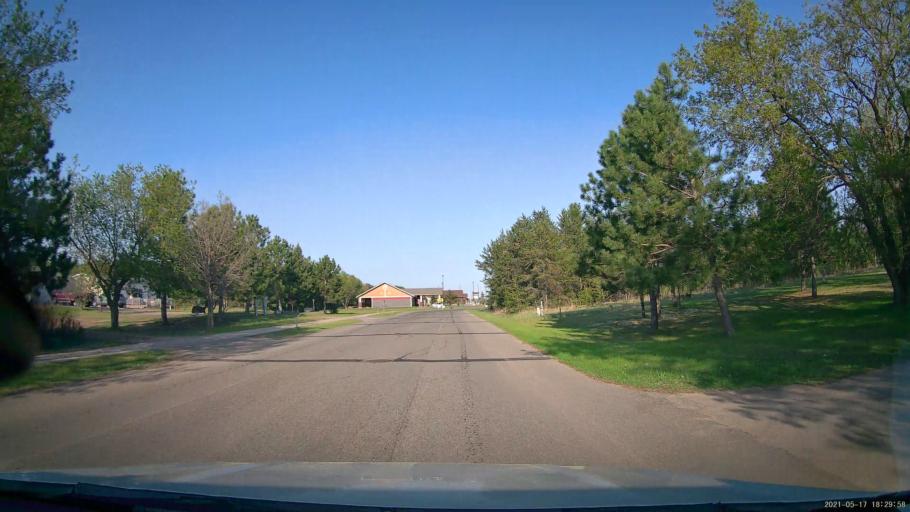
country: US
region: Minnesota
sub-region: Hubbard County
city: Park Rapids
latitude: 46.9251
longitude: -95.0435
